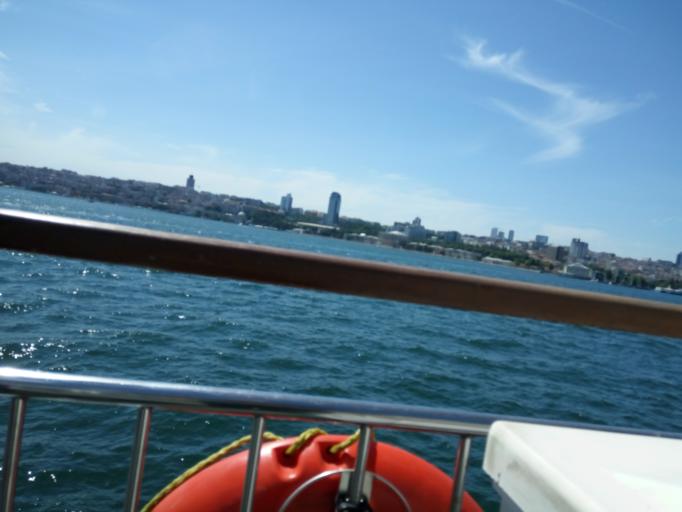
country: TR
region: Istanbul
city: UEskuedar
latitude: 41.0333
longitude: 29.0140
